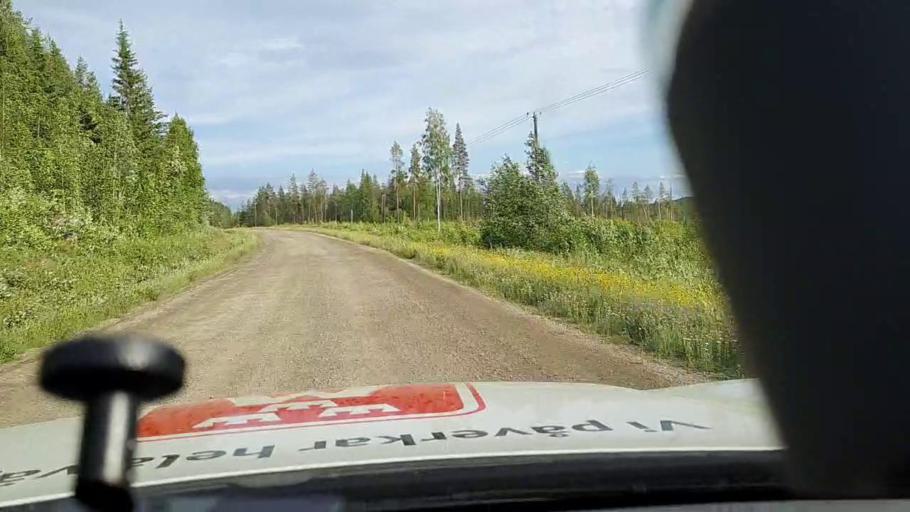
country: SE
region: Norrbotten
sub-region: Alvsbyns Kommun
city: AElvsbyn
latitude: 66.1823
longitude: 21.2198
